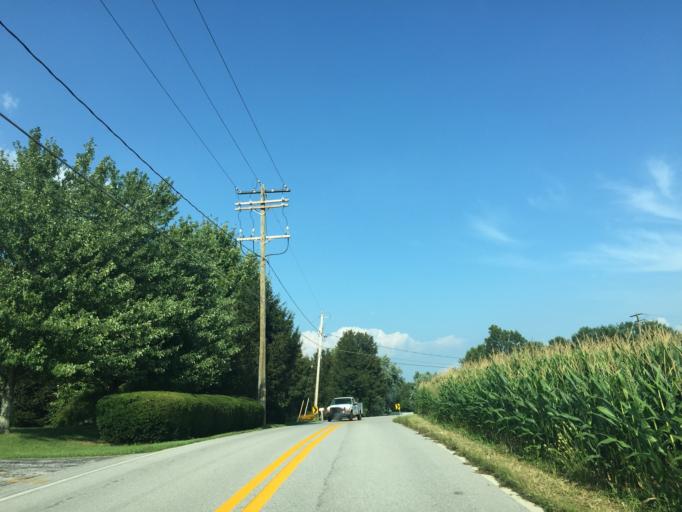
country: US
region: Maryland
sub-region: Carroll County
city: Hampstead
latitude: 39.6507
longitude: -76.8386
